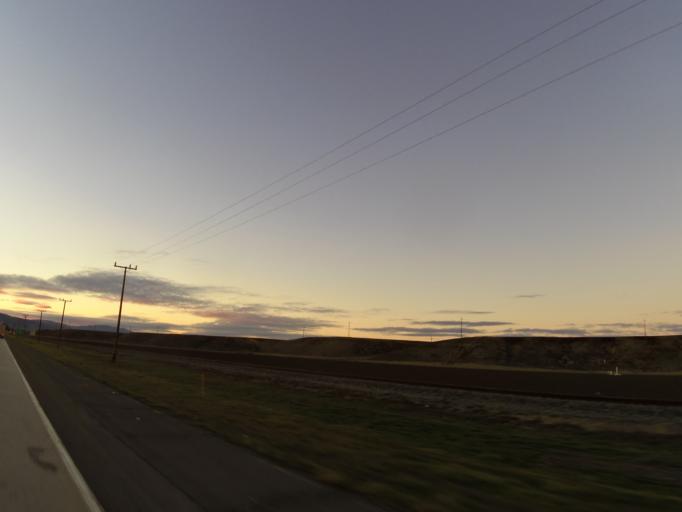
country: US
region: California
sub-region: Monterey County
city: King City
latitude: 36.1959
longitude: -121.0947
